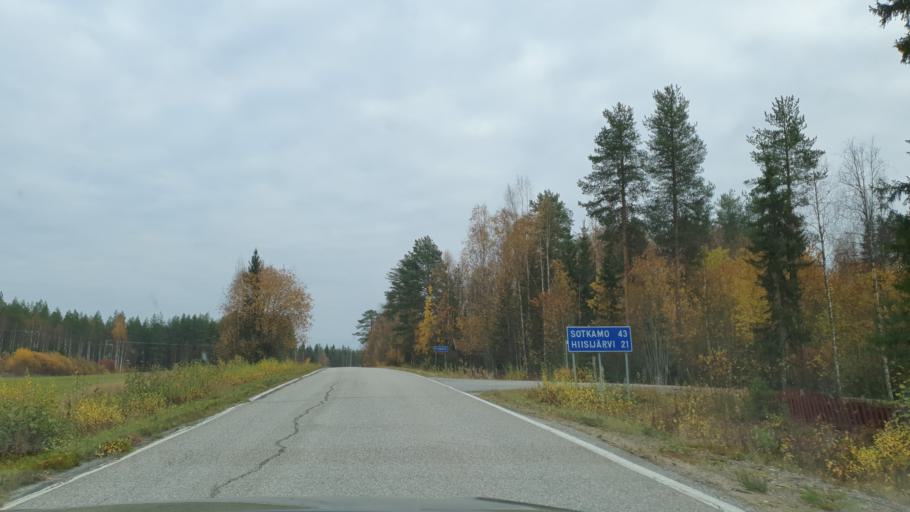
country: FI
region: Kainuu
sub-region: Kajaani
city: Ristijaervi
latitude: 64.4582
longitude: 28.3231
